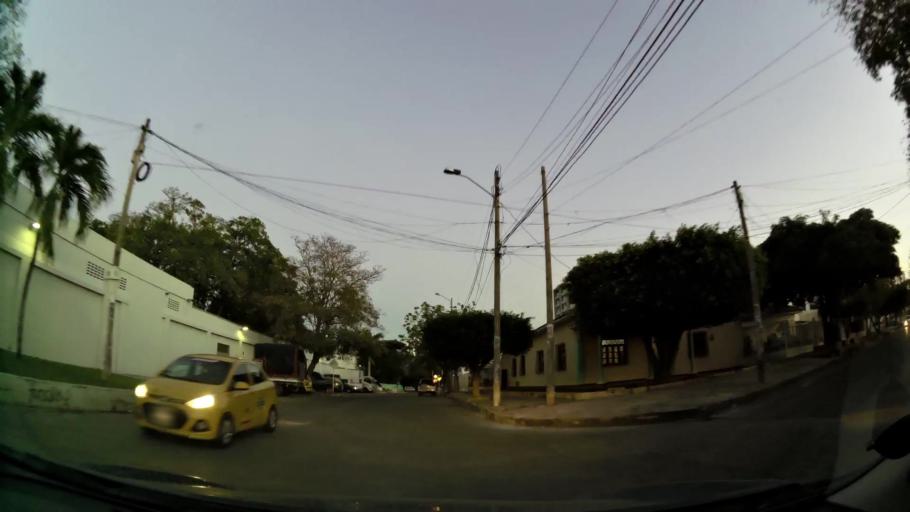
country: CO
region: Atlantico
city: Barranquilla
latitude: 10.9866
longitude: -74.7998
